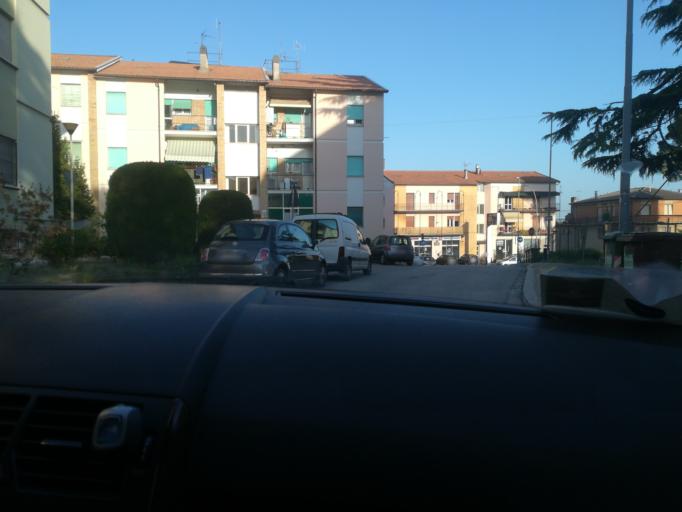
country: IT
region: The Marches
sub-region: Provincia di Macerata
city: Macerata
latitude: 43.2899
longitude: 13.4352
